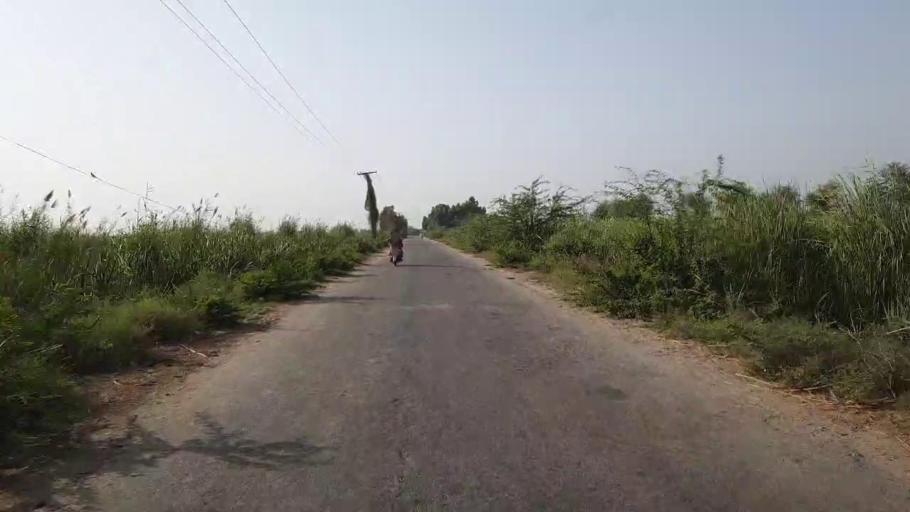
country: PK
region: Sindh
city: Jam Sahib
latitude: 26.4041
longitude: 68.8774
